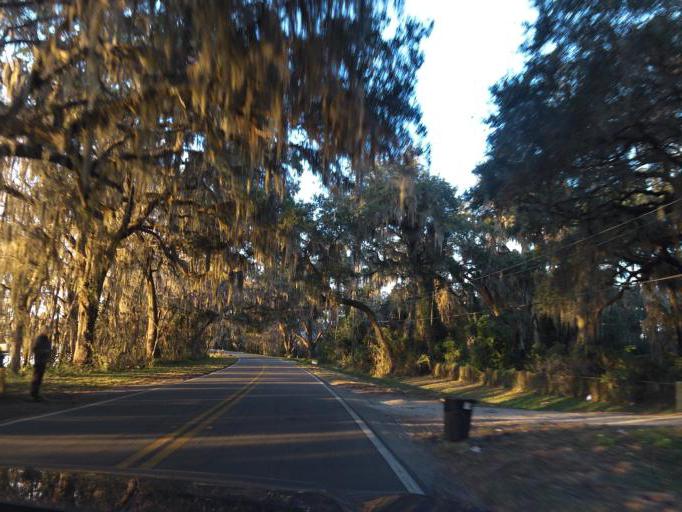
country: US
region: Florida
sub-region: Clay County
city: Green Cove Springs
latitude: 29.9119
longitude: -81.5918
